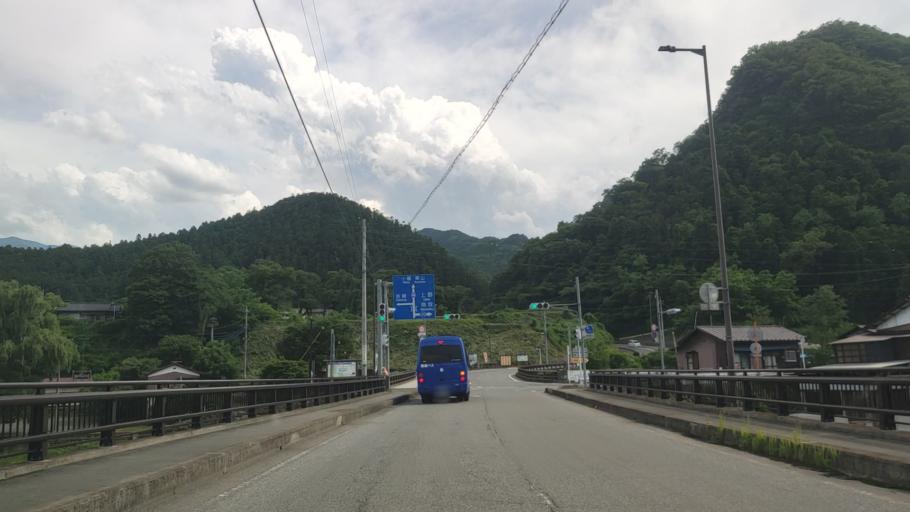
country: JP
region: Gunma
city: Tomioka
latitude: 36.2085
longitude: 138.7831
